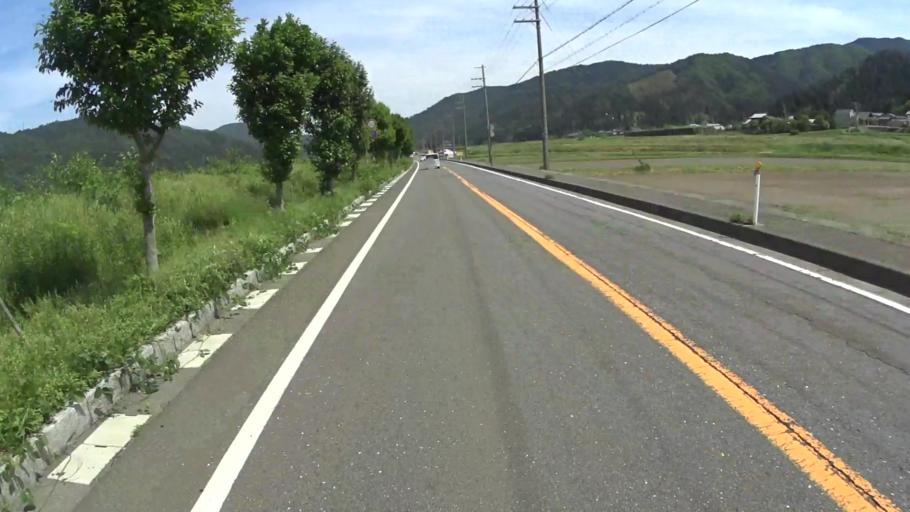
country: JP
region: Fukui
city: Obama
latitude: 35.4578
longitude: 135.8706
